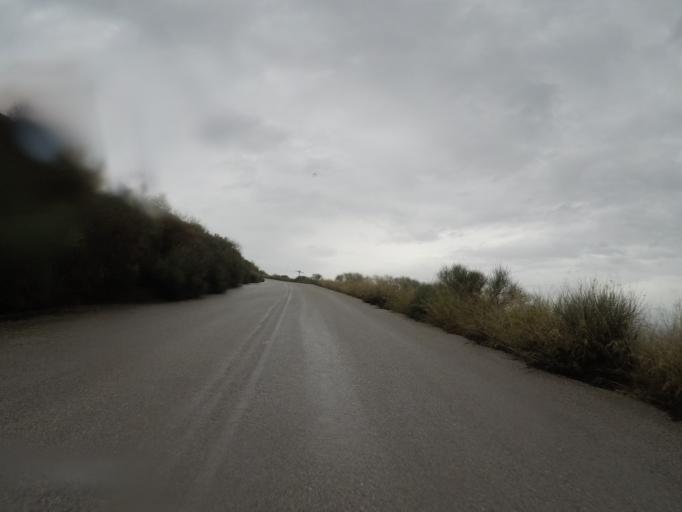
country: GR
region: Peloponnese
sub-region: Nomos Korinthias
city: Arkhaia Korinthos
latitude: 37.8960
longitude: 22.8694
